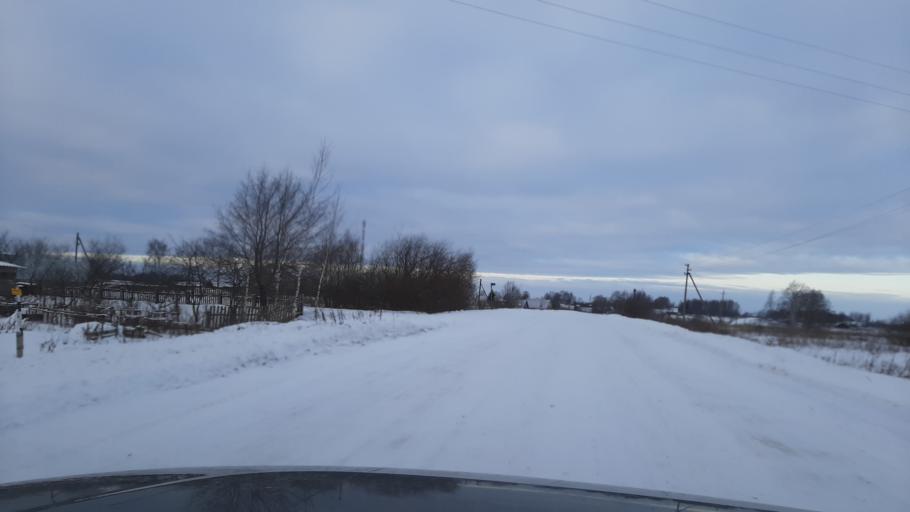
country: RU
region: Kostroma
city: Kosmynino
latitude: 57.4477
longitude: 40.9138
